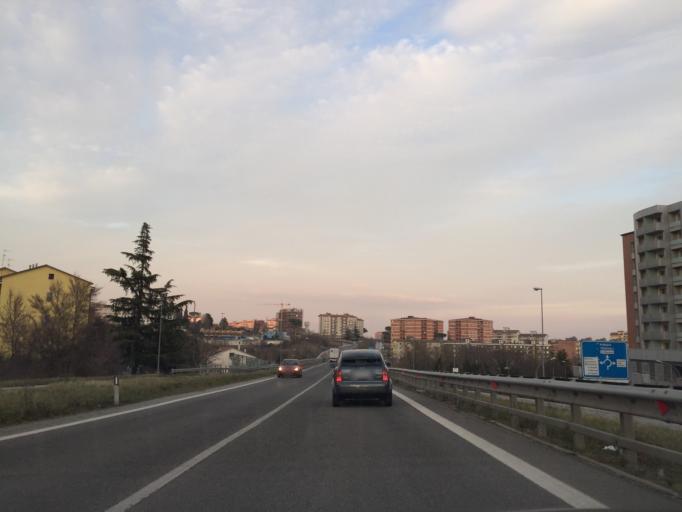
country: IT
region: Molise
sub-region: Provincia di Campobasso
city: Campobasso
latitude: 41.5552
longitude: 14.6648
